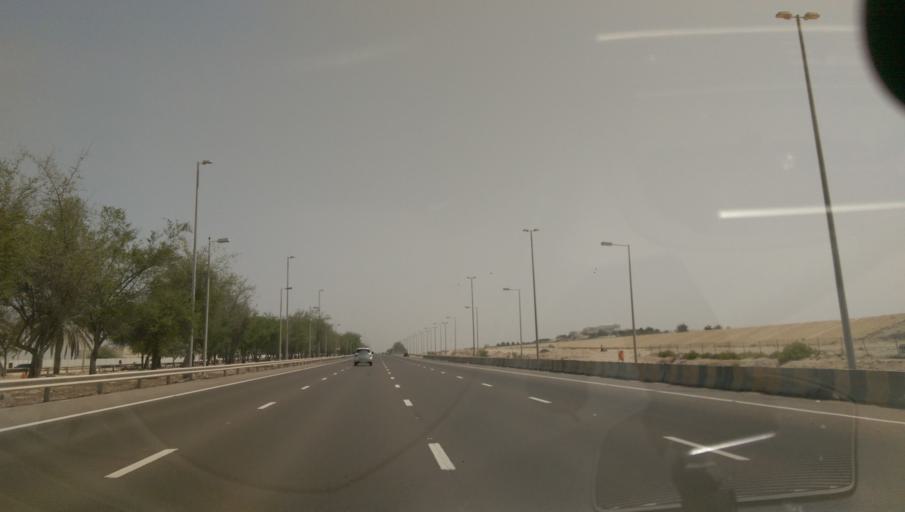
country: AE
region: Abu Dhabi
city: Abu Dhabi
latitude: 24.4327
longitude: 54.6781
